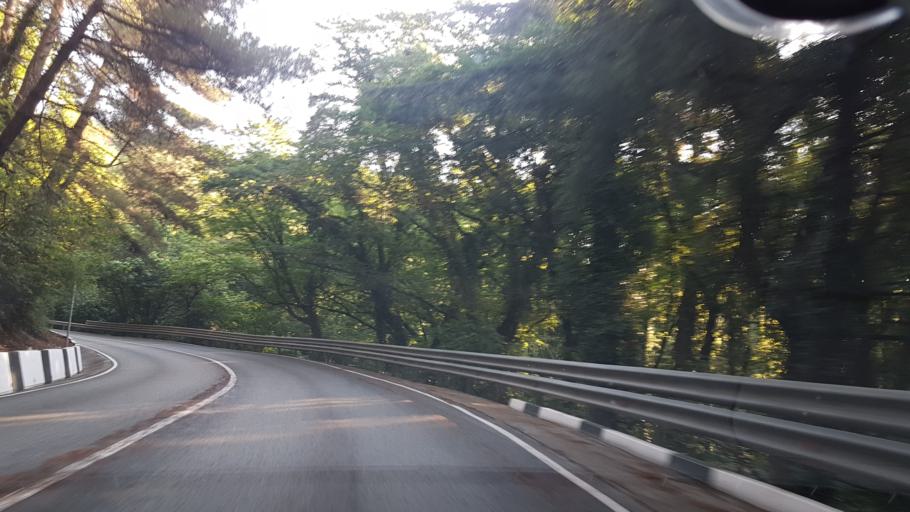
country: RU
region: Krasnodarskiy
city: Gornoye Loo
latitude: 43.6682
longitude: 39.6151
